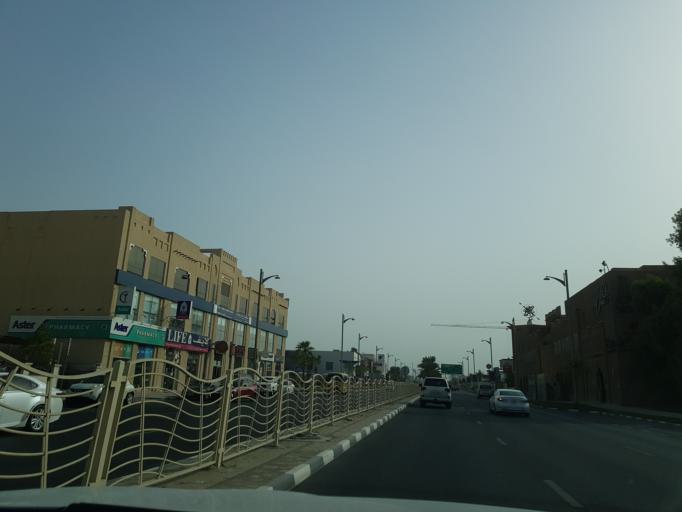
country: AE
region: Dubai
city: Dubai
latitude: 25.1630
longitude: 55.2105
